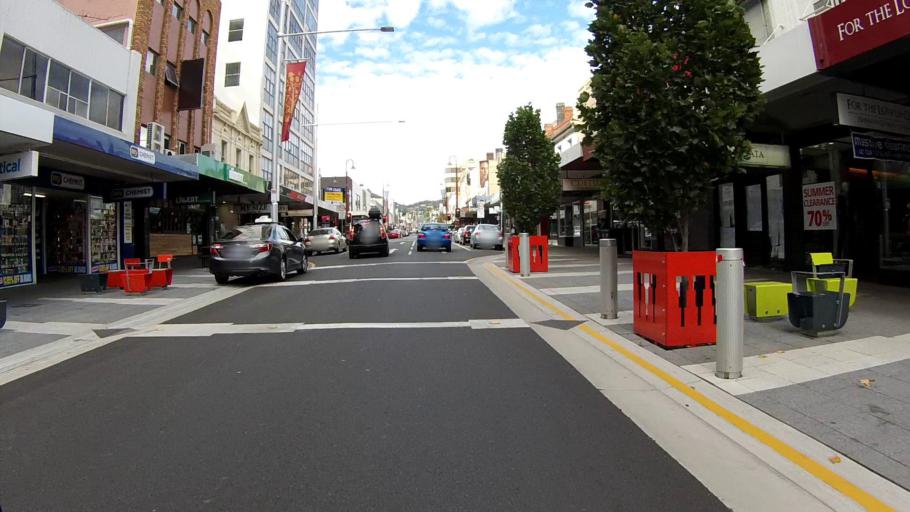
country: AU
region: Tasmania
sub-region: Hobart
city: Hobart
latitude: -42.8821
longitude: 147.3263
